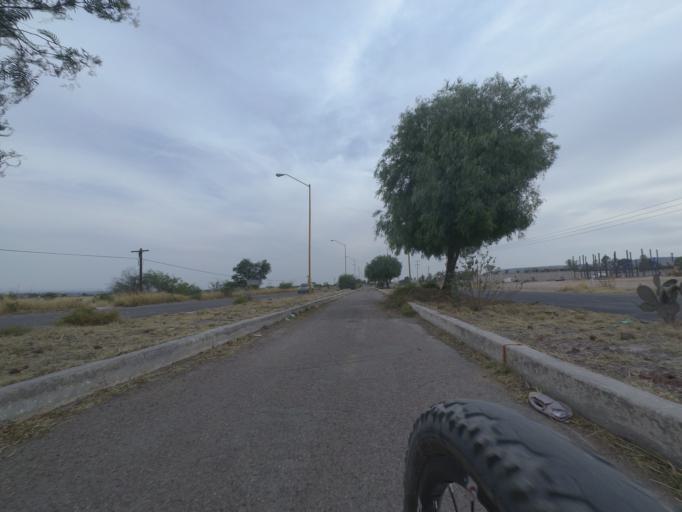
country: MX
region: Aguascalientes
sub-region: Aguascalientes
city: La Loma de los Negritos
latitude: 21.8741
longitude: -102.3701
